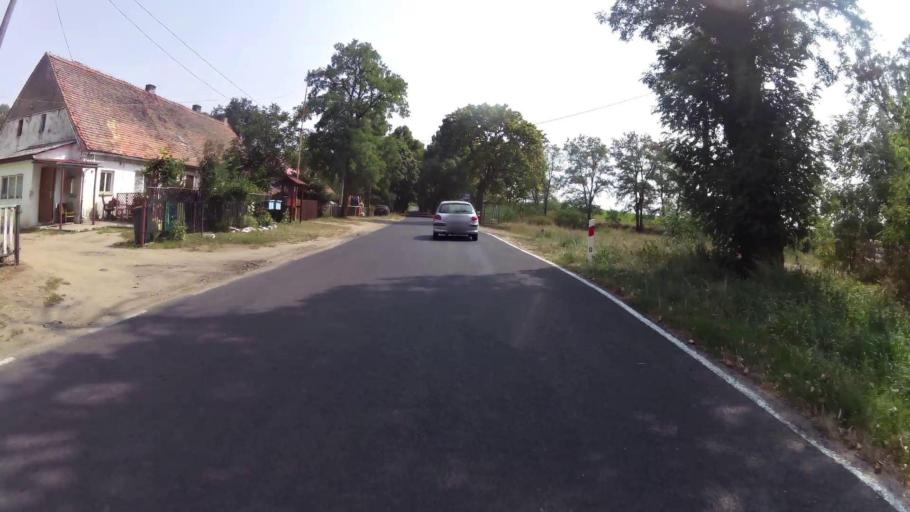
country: PL
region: West Pomeranian Voivodeship
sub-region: Powiat gryfinski
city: Moryn
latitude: 52.8231
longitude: 14.4293
